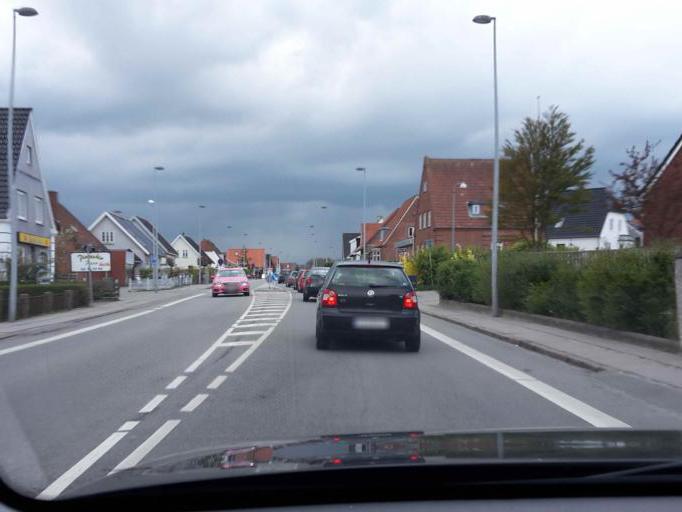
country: DK
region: South Denmark
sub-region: Odense Kommune
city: Odense
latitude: 55.4074
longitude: 10.3478
